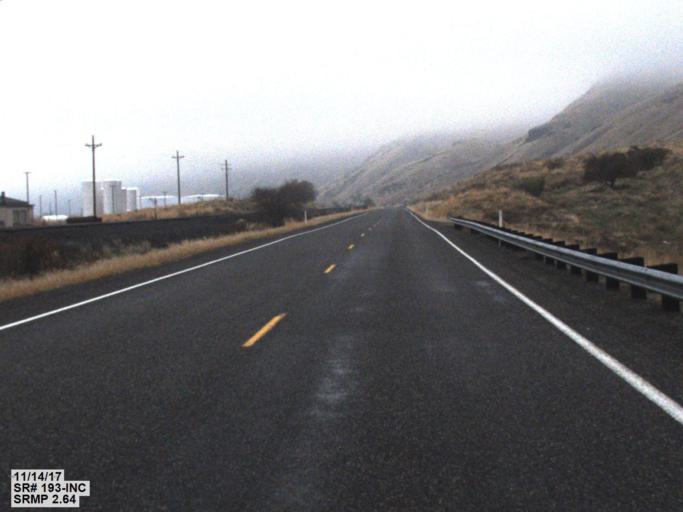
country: US
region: Washington
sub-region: Asotin County
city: Clarkston Heights-Vineland
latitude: 46.4284
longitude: -117.1168
